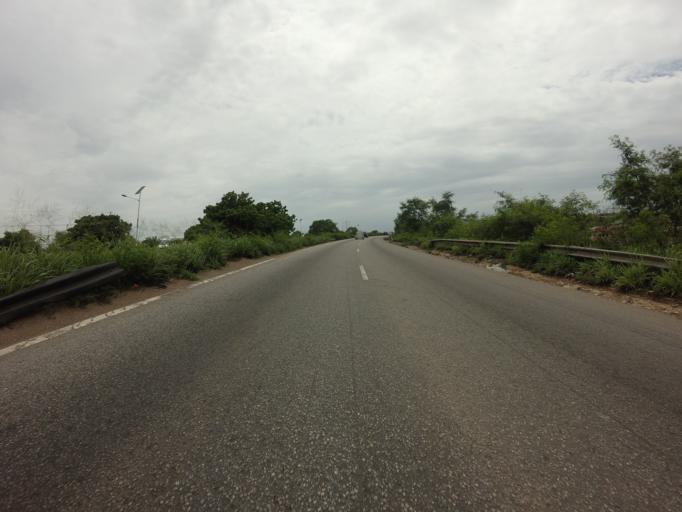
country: GH
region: Greater Accra
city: Dome
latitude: 5.6620
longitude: -0.2703
